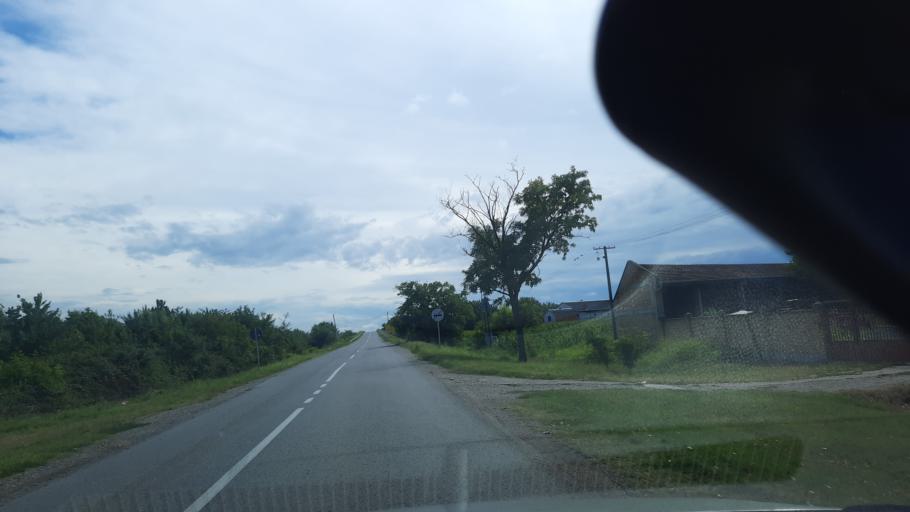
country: RS
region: Autonomna Pokrajina Vojvodina
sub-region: Sremski Okrug
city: Sremska Mitrovica
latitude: 45.0082
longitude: 19.6136
